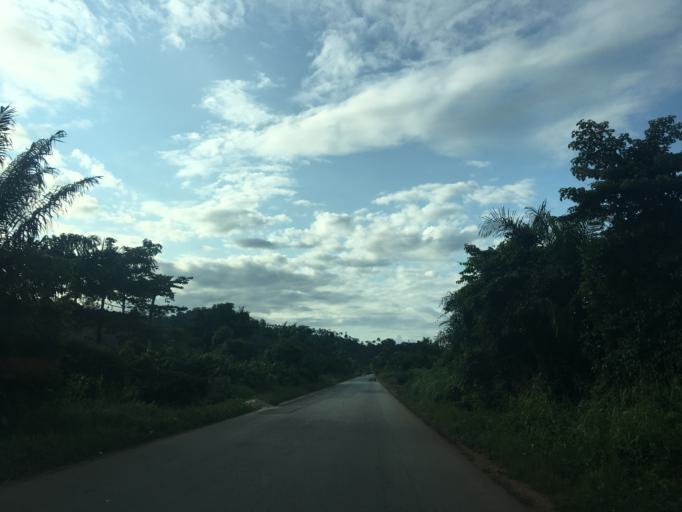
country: GH
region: Western
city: Bibiani
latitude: 6.2575
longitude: -2.2251
